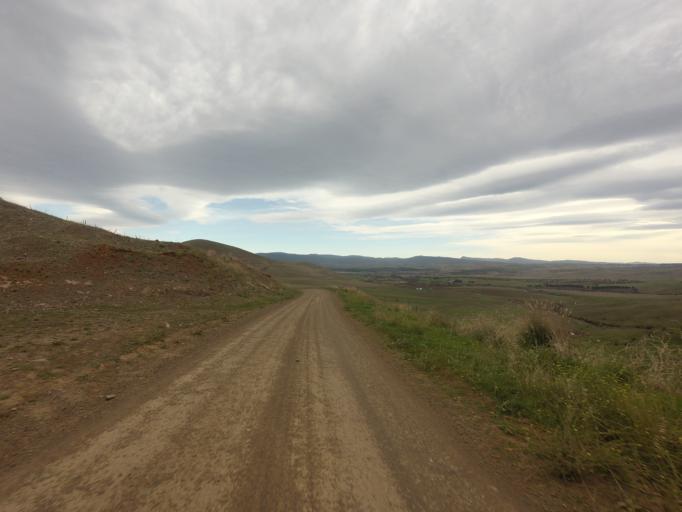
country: AU
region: Tasmania
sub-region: Derwent Valley
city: New Norfolk
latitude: -42.4549
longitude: 146.7646
